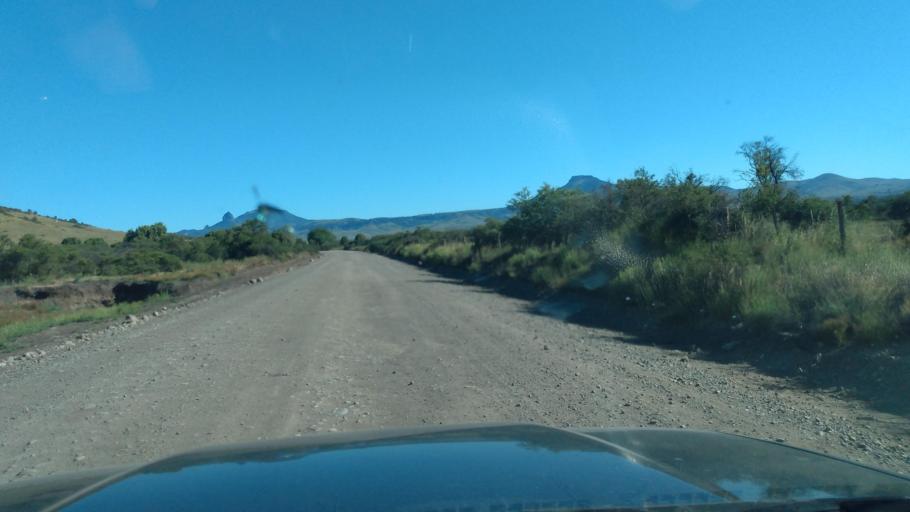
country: AR
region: Neuquen
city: Junin de los Andes
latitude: -39.8426
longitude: -71.1885
